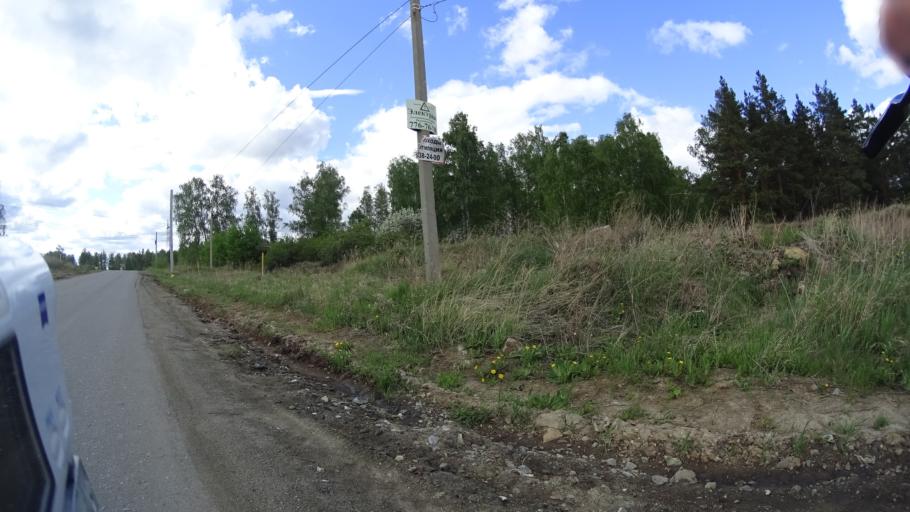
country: RU
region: Chelyabinsk
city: Sargazy
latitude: 55.1618
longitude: 61.2518
